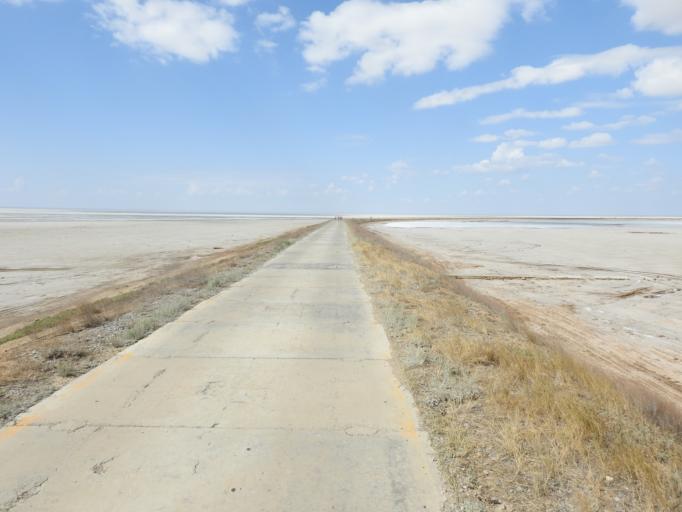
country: RU
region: Volgograd
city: El'ton
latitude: 49.1553
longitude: 46.8037
